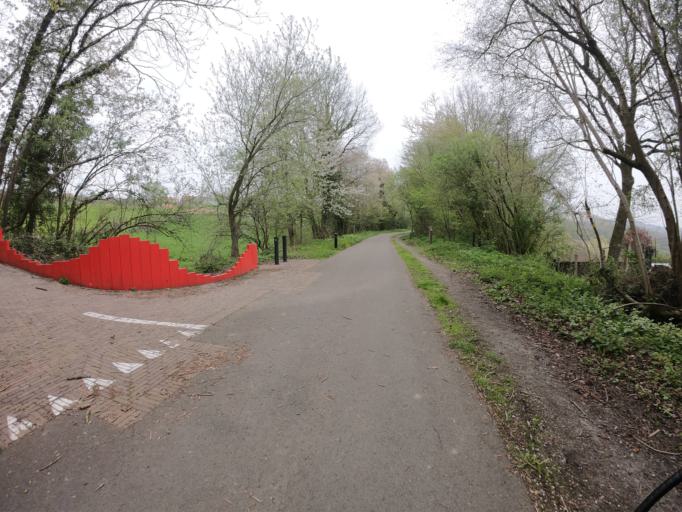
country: BE
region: Wallonia
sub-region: Province du Hainaut
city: Ellezelles
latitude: 50.7459
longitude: 3.6780
